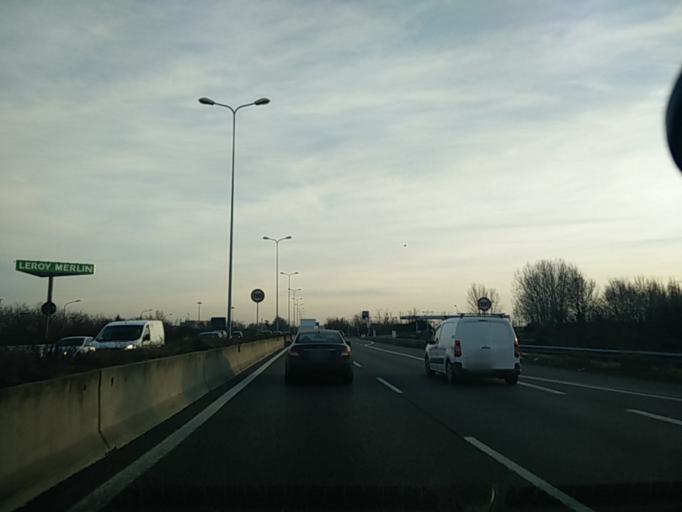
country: IT
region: Lombardy
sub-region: Provincia di Monza e Brianza
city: Varedo
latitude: 45.5904
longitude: 9.1735
